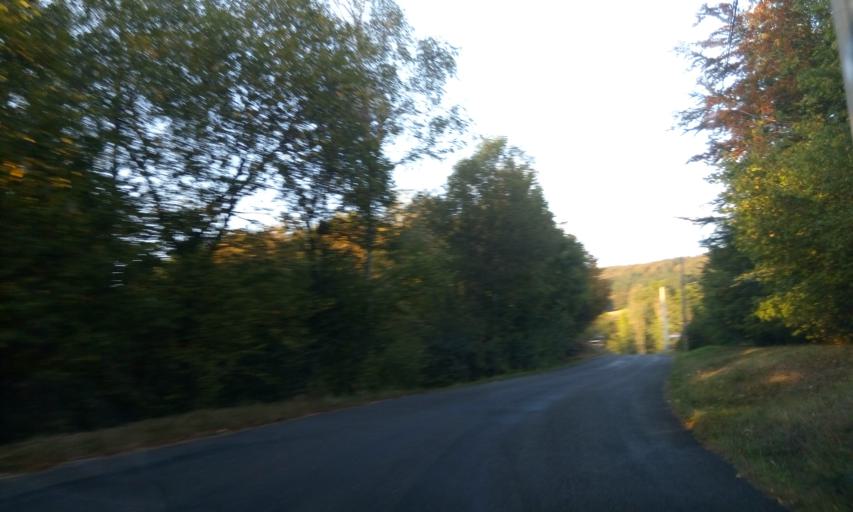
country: FR
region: Rhone-Alpes
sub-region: Departement de l'Ain
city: Nantua
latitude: 46.1790
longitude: 5.6837
